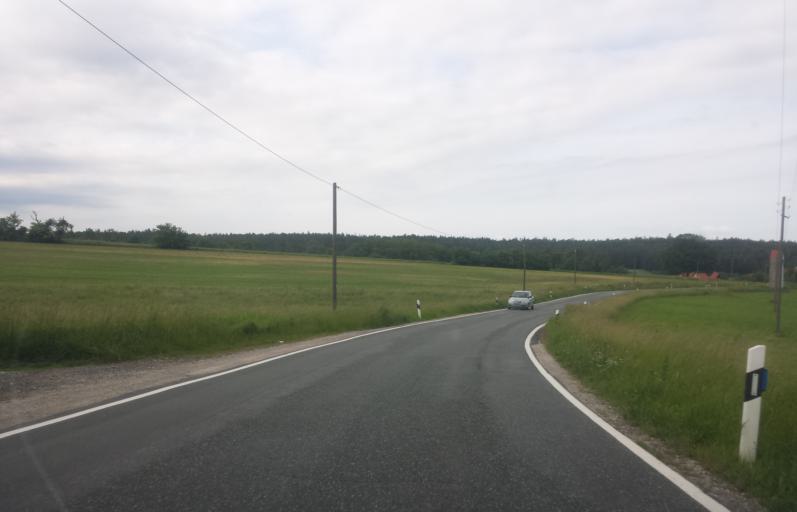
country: DE
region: Bavaria
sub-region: Upper Franconia
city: Schlusselfeld
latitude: 49.7836
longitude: 10.6554
